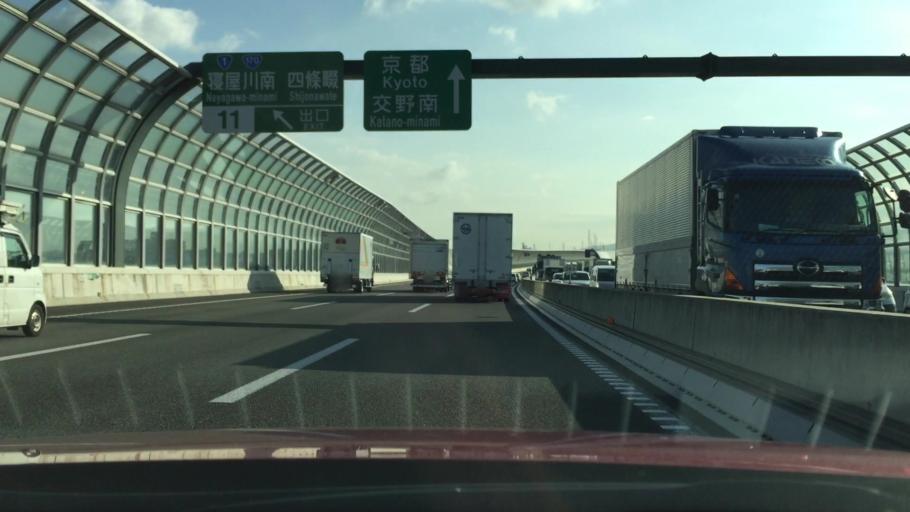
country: JP
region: Osaka
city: Neyagawa
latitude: 34.7420
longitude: 135.6175
